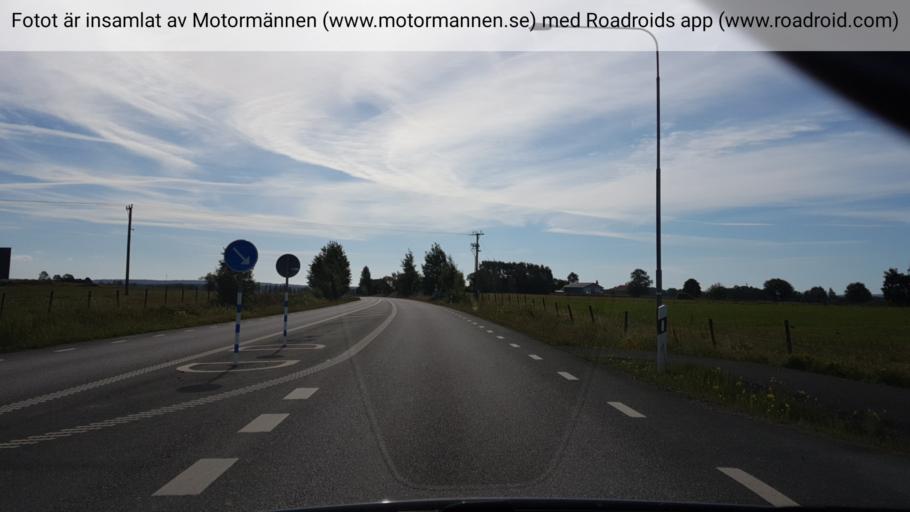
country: SE
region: Vaestra Goetaland
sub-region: Tidaholms Kommun
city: Olofstorp
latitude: 58.3537
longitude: 14.0518
